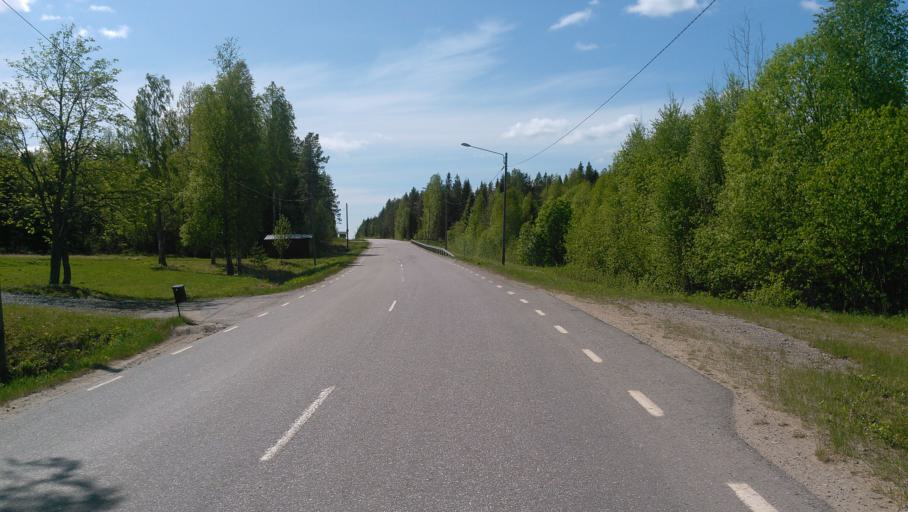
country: SE
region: Vaesterbotten
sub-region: Umea Kommun
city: Roback
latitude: 63.8630
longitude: 20.0121
